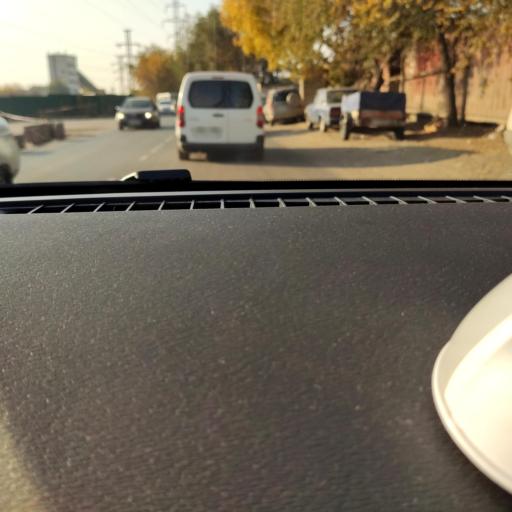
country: RU
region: Samara
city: Petra-Dubrava
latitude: 53.2530
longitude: 50.2933
